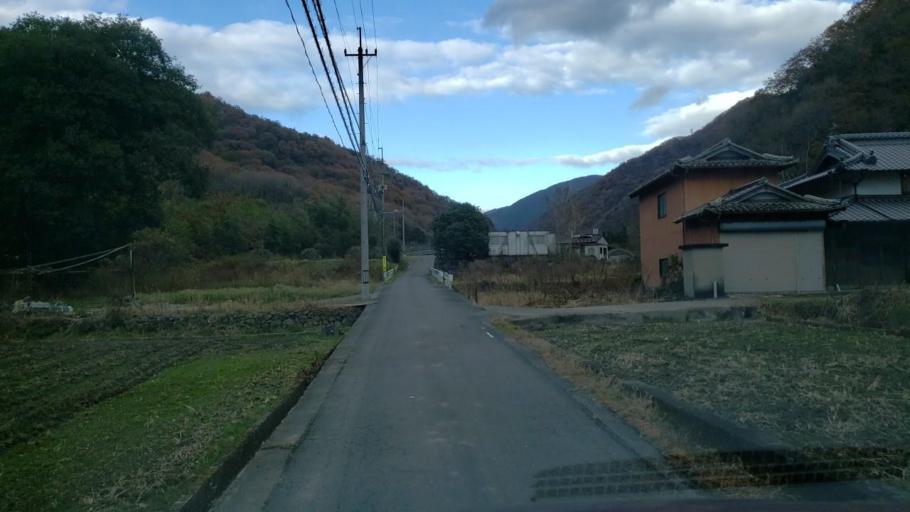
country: JP
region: Tokushima
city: Wakimachi
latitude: 34.1100
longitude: 134.2240
